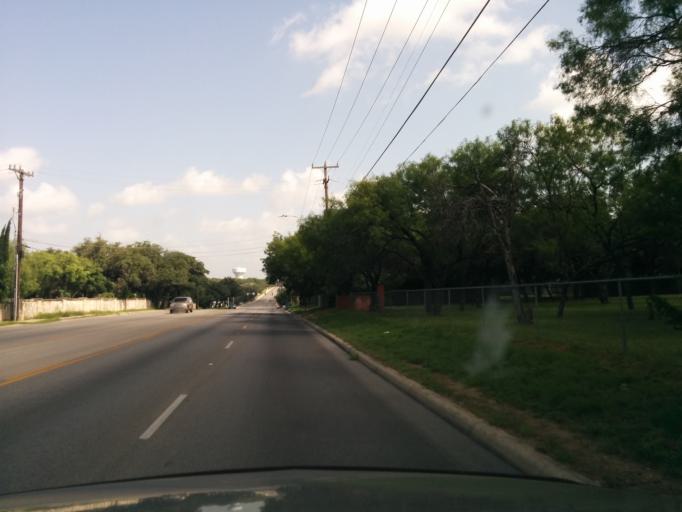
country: US
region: Texas
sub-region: Bexar County
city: Leon Valley
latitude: 29.5319
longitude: -98.6046
